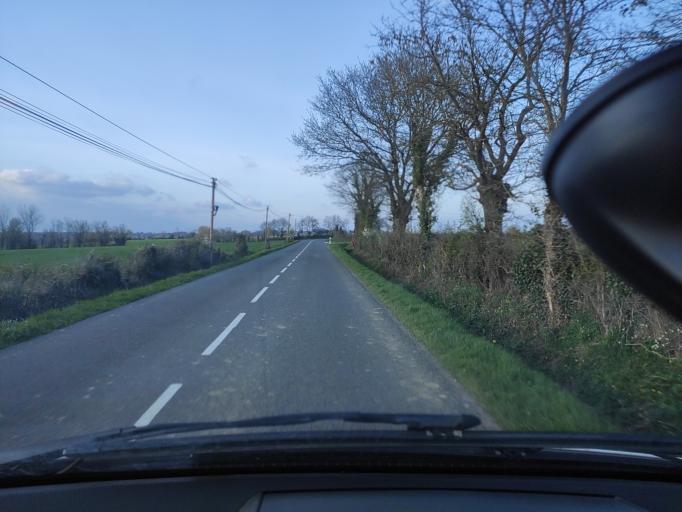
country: FR
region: Pays de la Loire
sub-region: Departement de la Vendee
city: La Chaize-le-Vicomte
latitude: 46.6441
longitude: -1.2985
